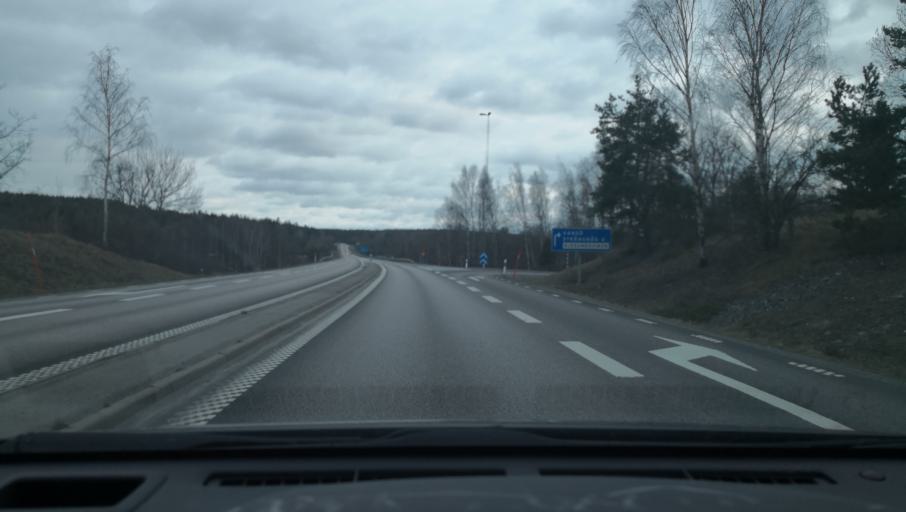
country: SE
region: Soedermanland
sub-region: Strangnas Kommun
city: Strangnas
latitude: 59.3883
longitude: 16.9896
